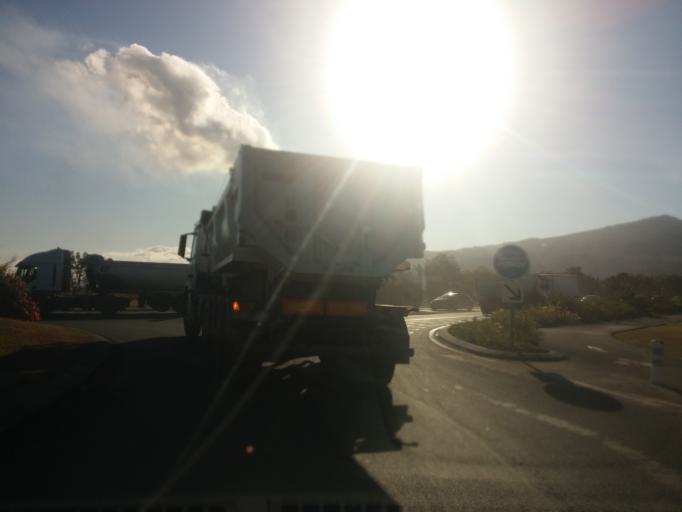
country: RE
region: Reunion
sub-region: Reunion
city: La Possession
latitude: -20.9451
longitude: 55.3177
